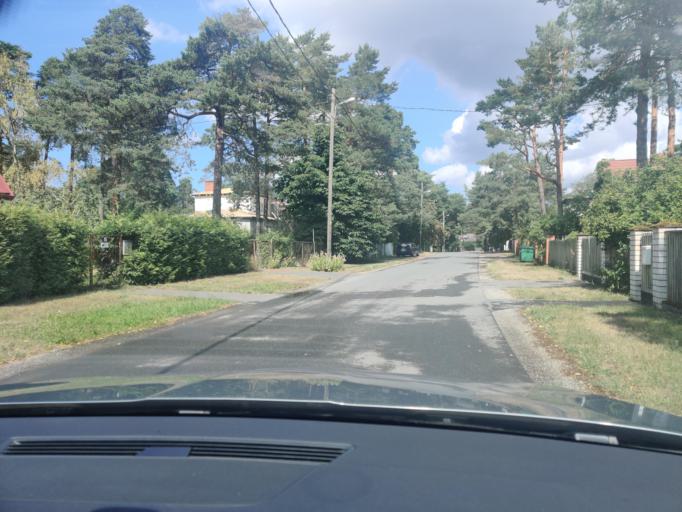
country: EE
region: Harju
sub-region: Saue vald
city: Laagri
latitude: 59.3667
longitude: 24.6276
